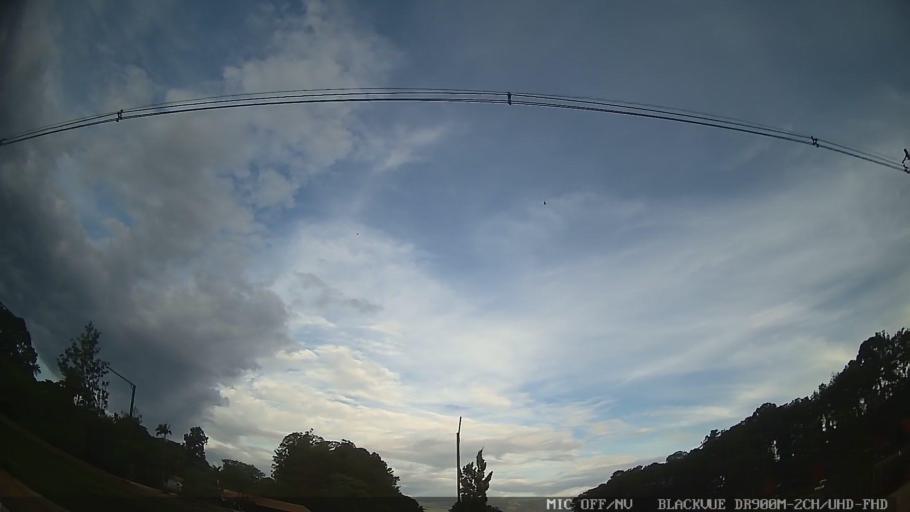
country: BR
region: Sao Paulo
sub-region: Jaguariuna
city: Jaguariuna
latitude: -22.6369
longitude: -47.0528
